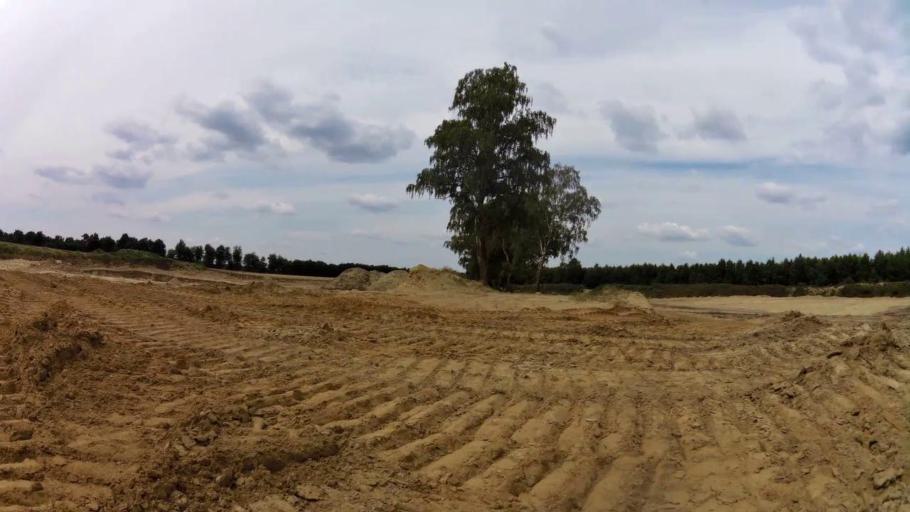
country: PL
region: West Pomeranian Voivodeship
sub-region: Powiat drawski
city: Drawsko Pomorskie
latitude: 53.5028
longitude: 15.7172
